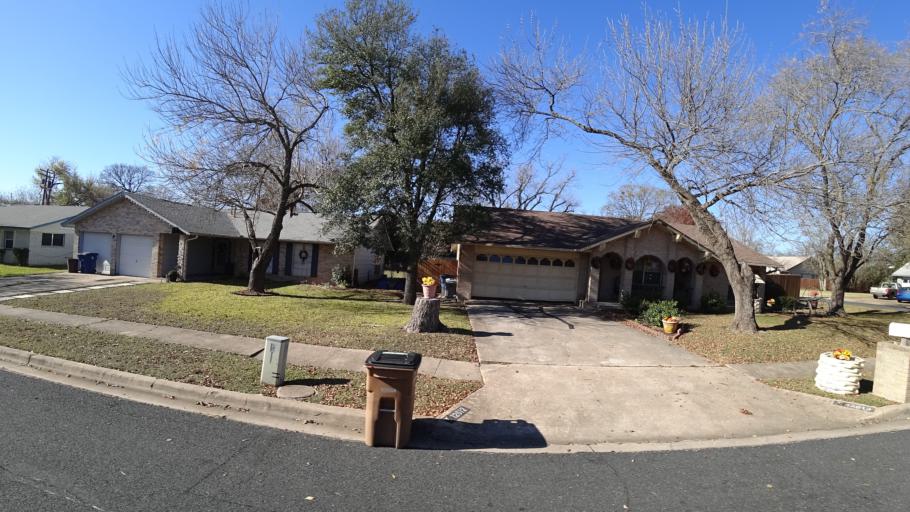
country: US
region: Texas
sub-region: Travis County
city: Wells Branch
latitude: 30.4201
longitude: -97.6963
